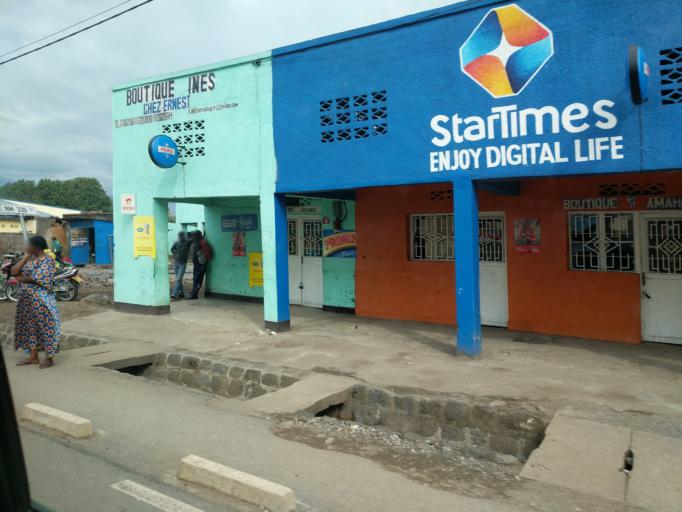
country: RW
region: Northern Province
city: Musanze
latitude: -1.4992
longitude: 29.6254
